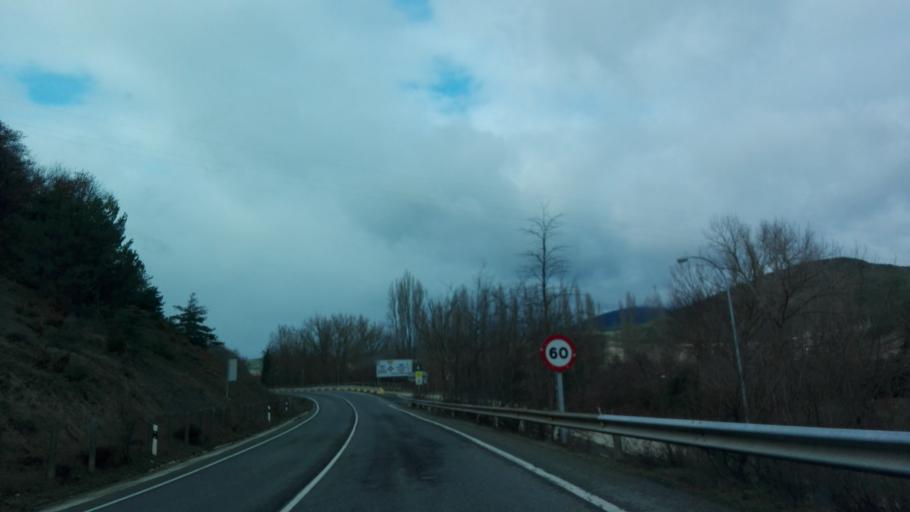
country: ES
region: Navarre
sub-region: Provincia de Navarra
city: Atarrabia
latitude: 42.8368
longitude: -1.6052
